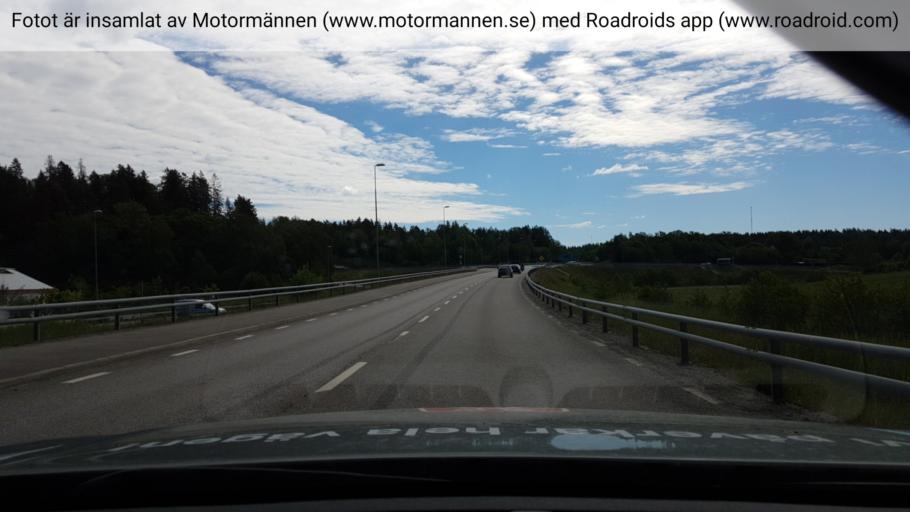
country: SE
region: Stockholm
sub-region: Nynashamns Kommun
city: Osmo
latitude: 58.9780
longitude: 17.9075
